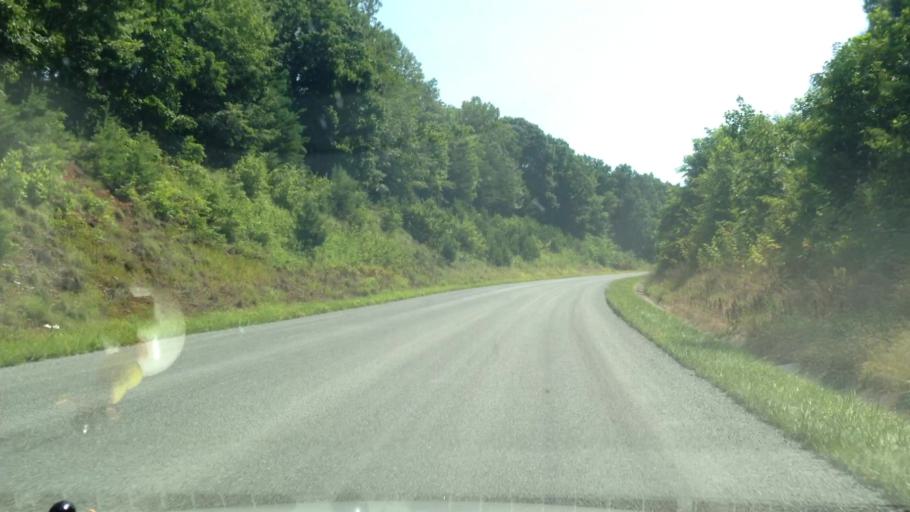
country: US
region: Virginia
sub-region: Patrick County
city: Stuart
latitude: 36.5987
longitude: -80.3046
